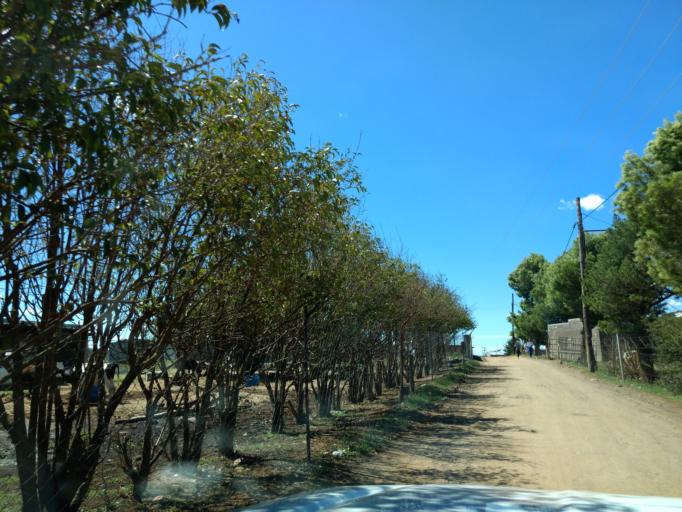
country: LS
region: Maseru
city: Maseru
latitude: -29.3690
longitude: 27.5121
